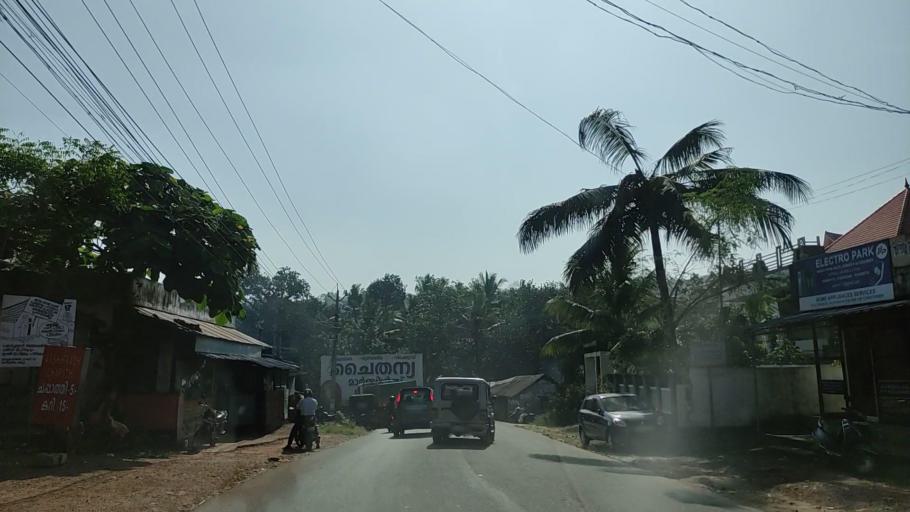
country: IN
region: Kerala
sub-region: Kollam
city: Punalur
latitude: 8.9150
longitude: 76.8876
